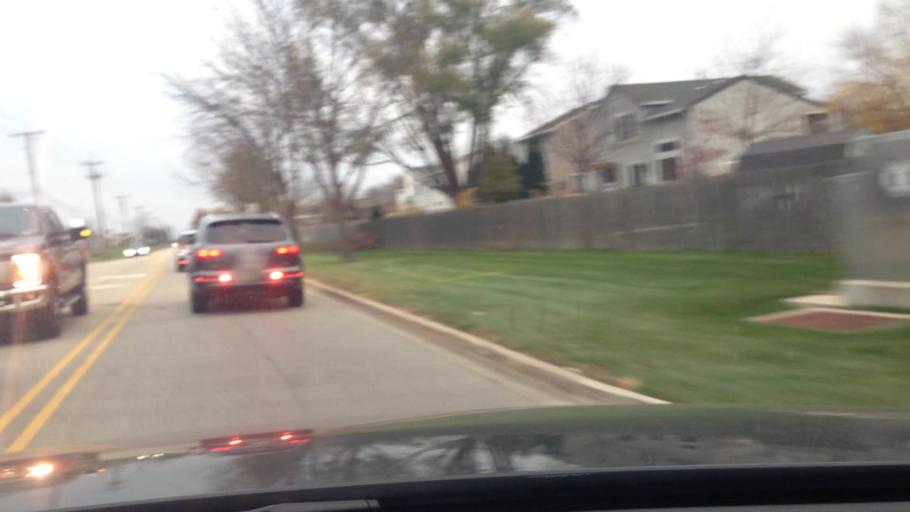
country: US
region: Illinois
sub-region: McHenry County
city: Huntley
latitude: 42.1830
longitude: -88.3839
